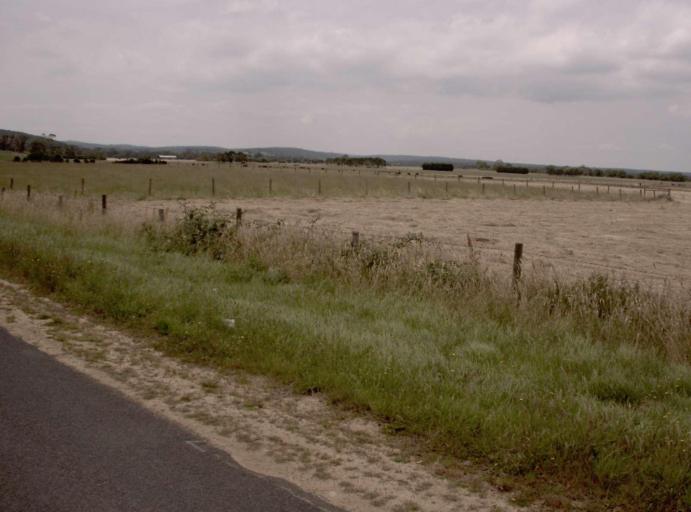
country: AU
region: Victoria
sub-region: Latrobe
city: Traralgon
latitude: -38.4955
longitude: 146.6789
